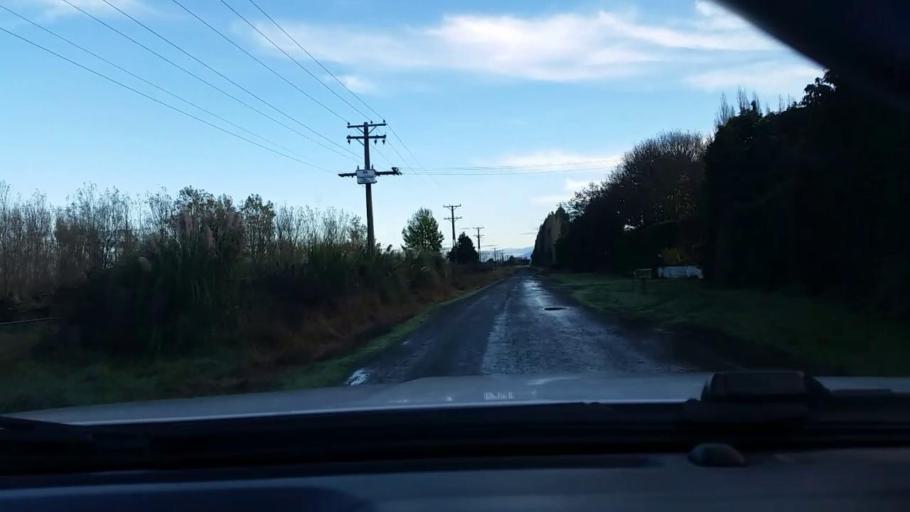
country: NZ
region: Southland
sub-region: Southland District
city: Winton
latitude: -46.1502
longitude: 168.2560
